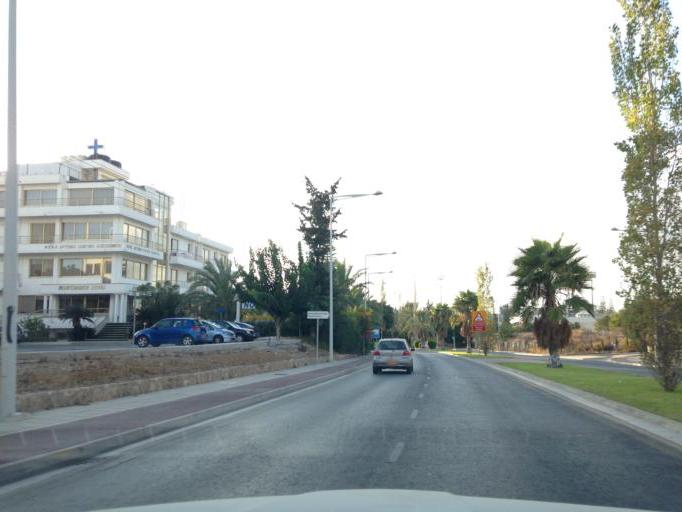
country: CY
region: Pafos
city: Paphos
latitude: 34.7670
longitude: 32.4437
